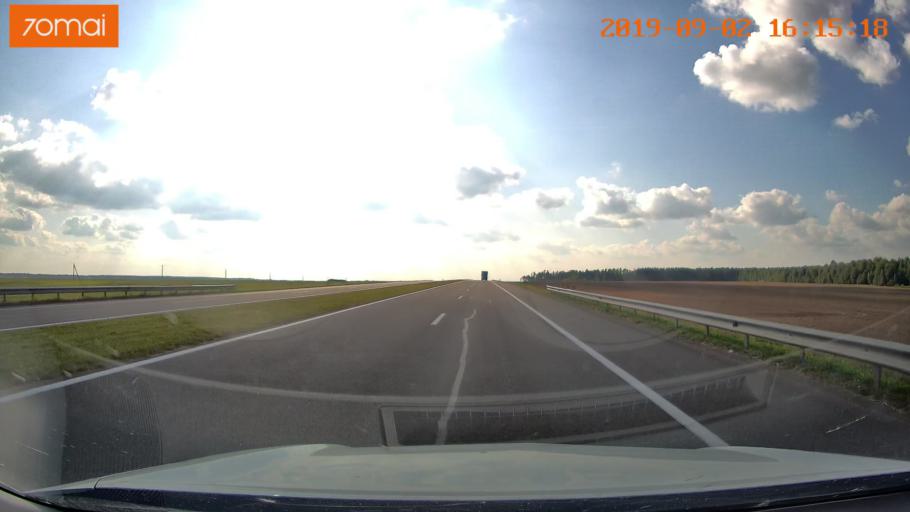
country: BY
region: Minsk
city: Chervyen'
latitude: 53.7392
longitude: 28.5331
